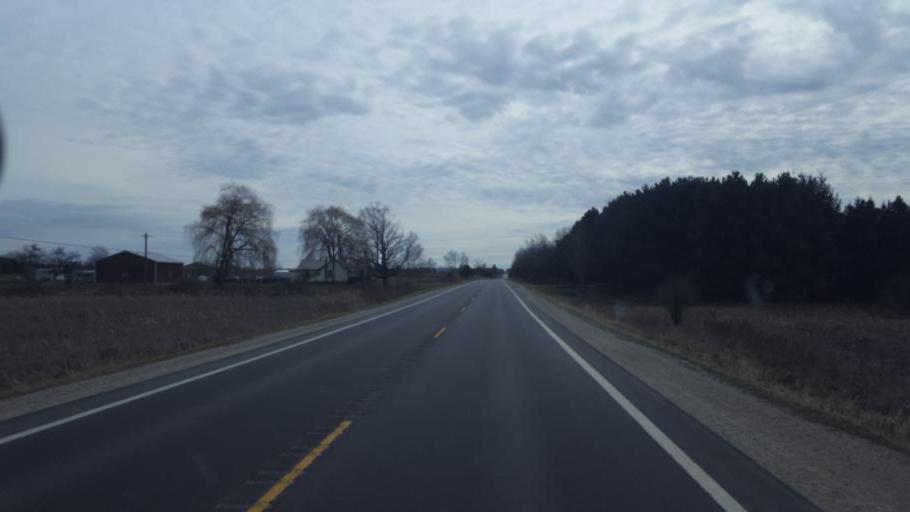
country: US
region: Michigan
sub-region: Isabella County
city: Lake Isabella
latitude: 43.7214
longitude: -85.1468
